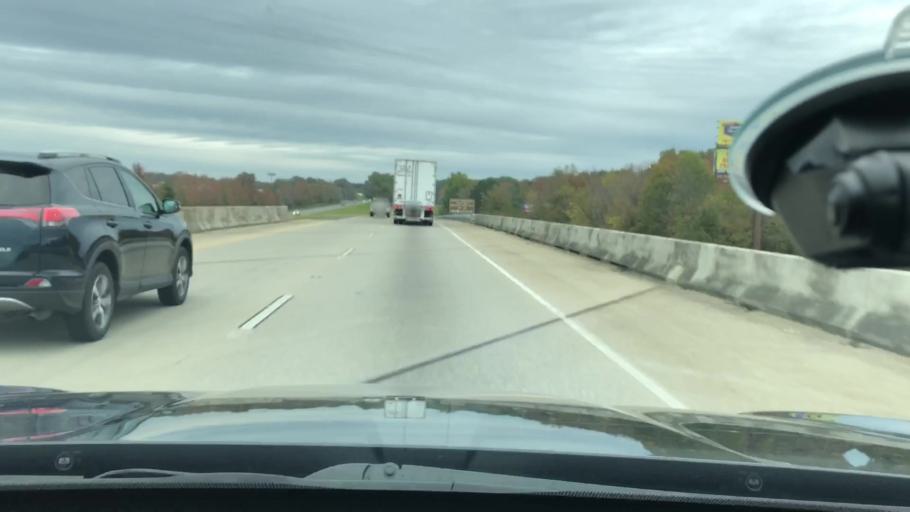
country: US
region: Arkansas
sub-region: Hempstead County
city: Hope
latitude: 33.6751
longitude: -93.6197
